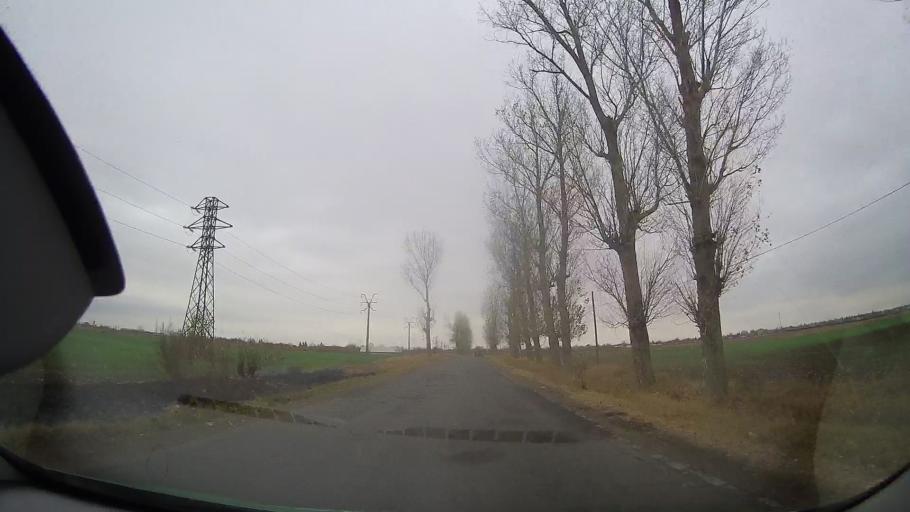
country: RO
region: Buzau
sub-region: Comuna Rusetu
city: Rusetu
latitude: 44.9508
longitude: 27.2242
